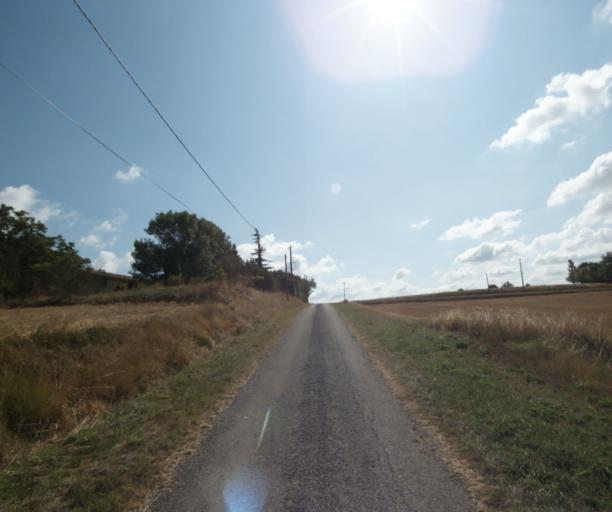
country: FR
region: Midi-Pyrenees
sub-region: Departement de la Haute-Garonne
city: Auriac-sur-Vendinelle
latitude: 43.4559
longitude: 1.8167
